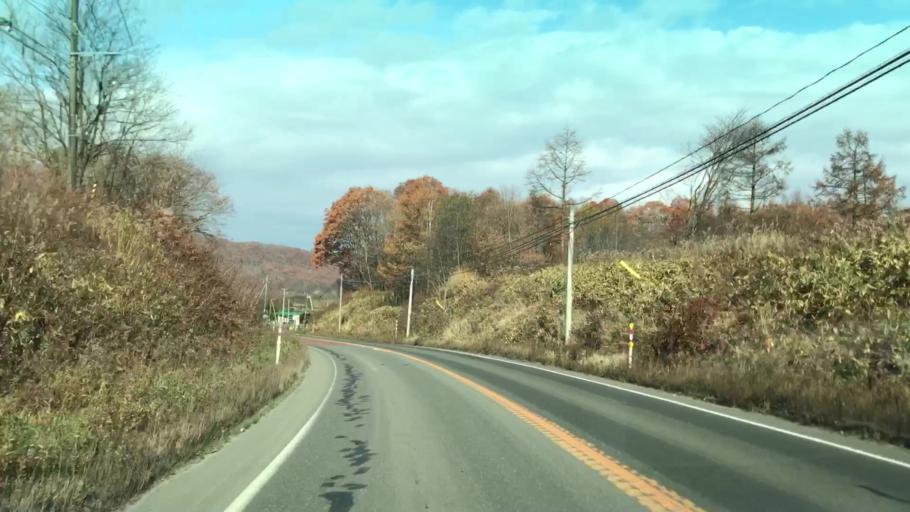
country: JP
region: Hokkaido
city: Shizunai-furukawacho
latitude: 42.6093
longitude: 142.1480
